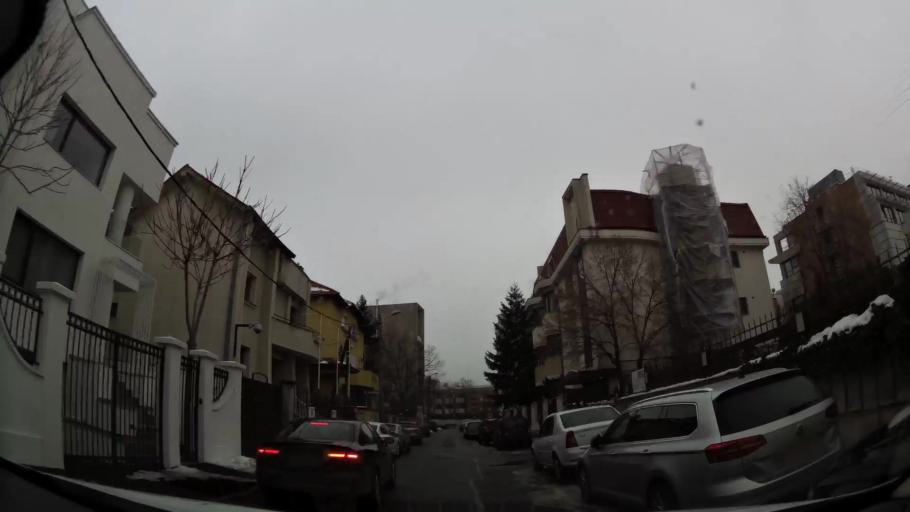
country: RO
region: Bucuresti
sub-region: Municipiul Bucuresti
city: Bucharest
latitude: 44.4775
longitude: 26.0900
